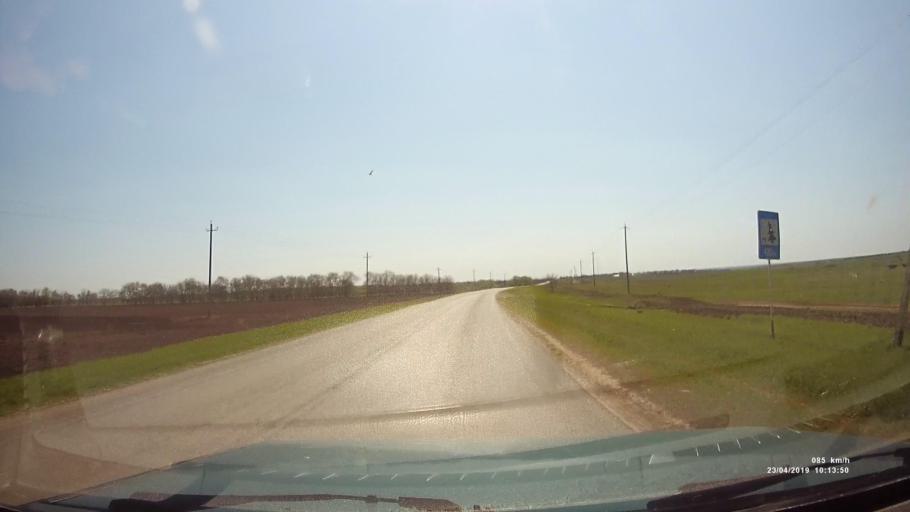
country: RU
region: Rostov
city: Sovetskoye
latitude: 46.6825
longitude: 42.3625
